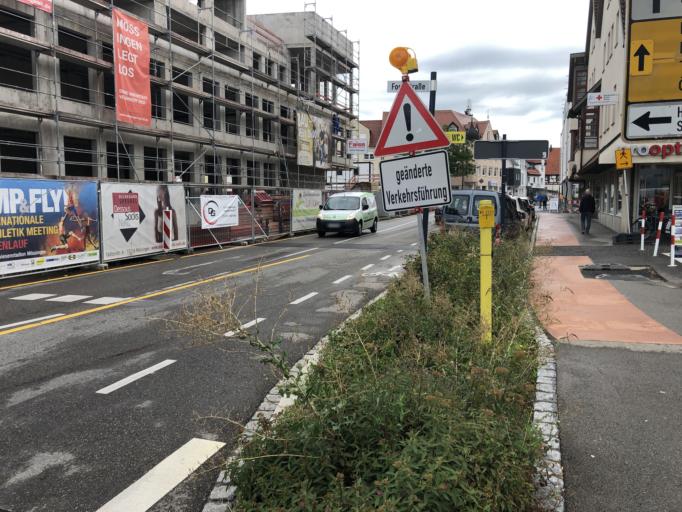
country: DE
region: Baden-Wuerttemberg
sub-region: Tuebingen Region
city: Mossingen
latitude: 48.4058
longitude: 9.0568
